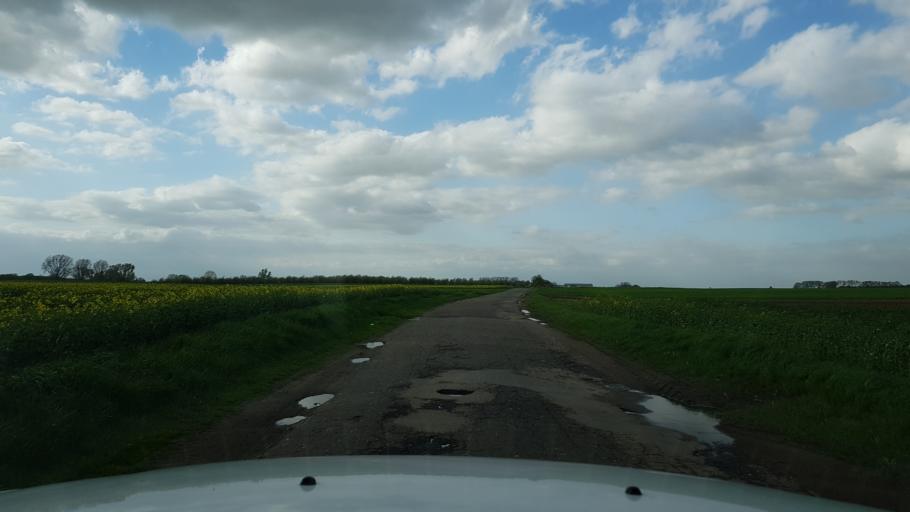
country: PL
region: West Pomeranian Voivodeship
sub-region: Powiat pyrzycki
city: Przelewice
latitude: 53.0565
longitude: 15.1099
